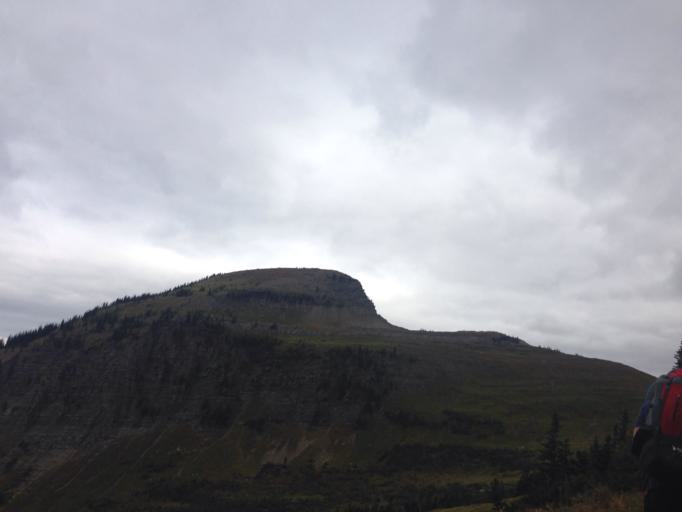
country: US
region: Montana
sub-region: Flathead County
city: Columbia Falls
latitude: 48.7289
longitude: -113.7186
